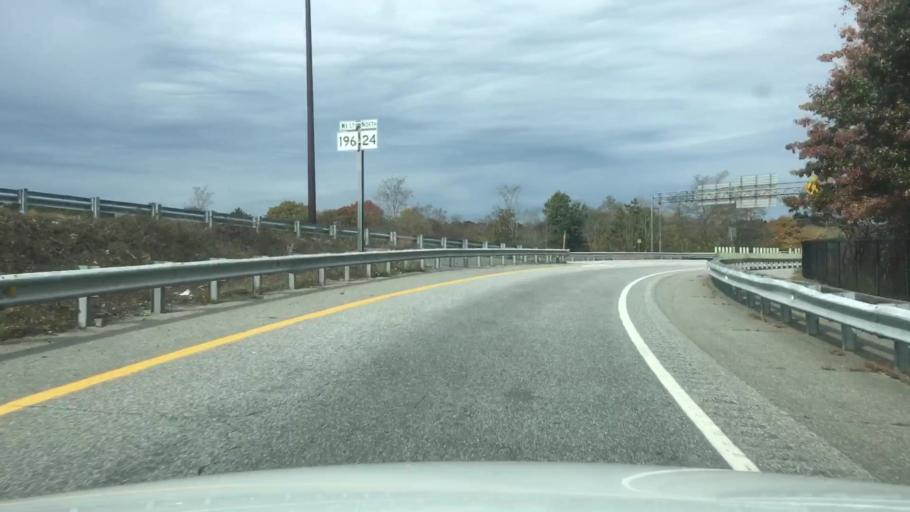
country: US
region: Maine
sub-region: Cumberland County
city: Brunswick
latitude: 43.9200
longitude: -69.9527
